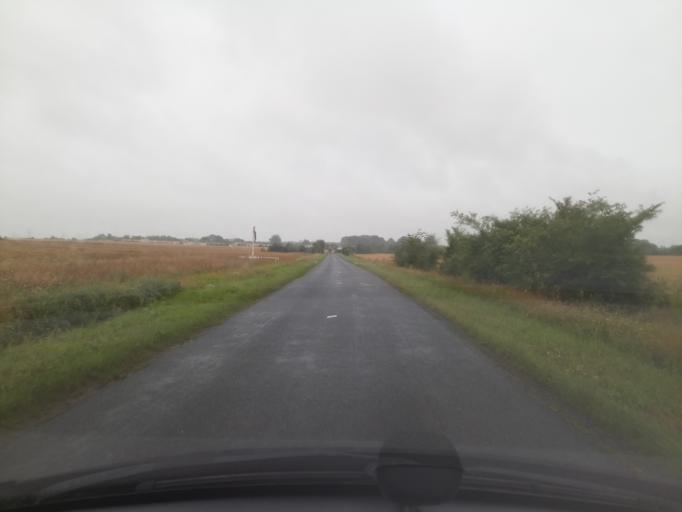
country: FR
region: Poitou-Charentes
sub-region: Departement de la Charente-Maritime
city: Verines
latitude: 46.2266
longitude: -0.9797
